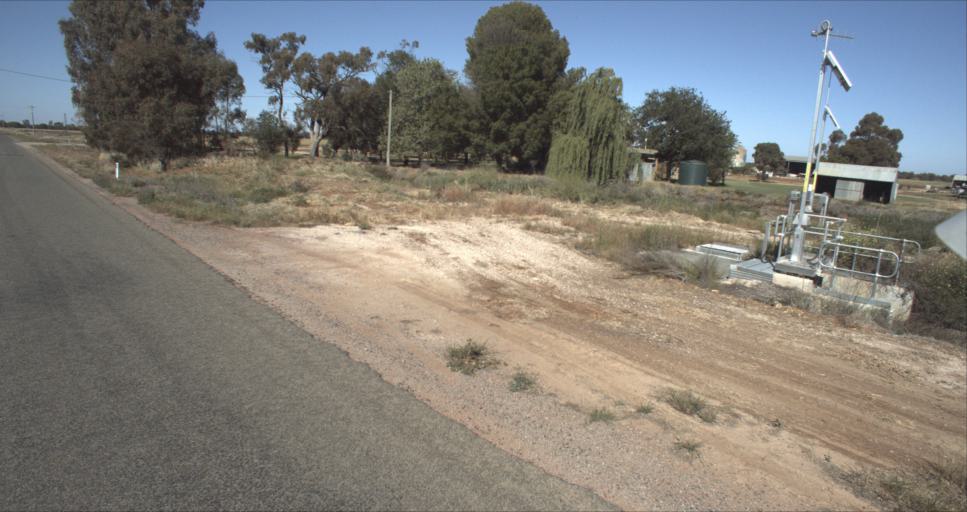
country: AU
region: New South Wales
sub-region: Leeton
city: Leeton
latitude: -34.5546
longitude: 146.2667
